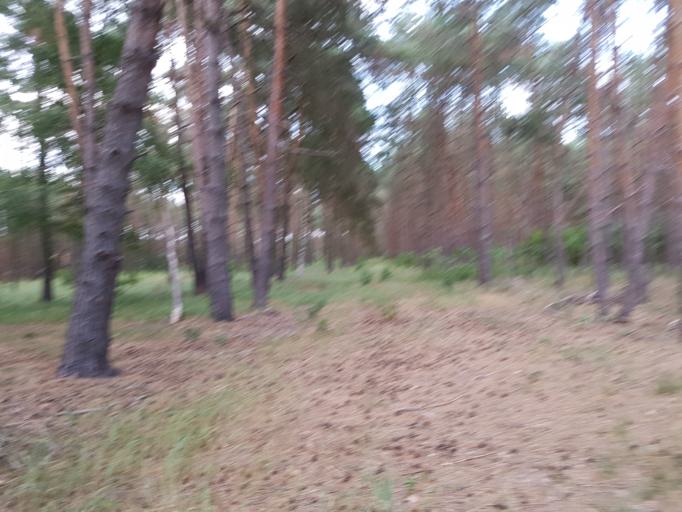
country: DE
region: Brandenburg
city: Schilda
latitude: 51.5610
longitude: 13.3528
